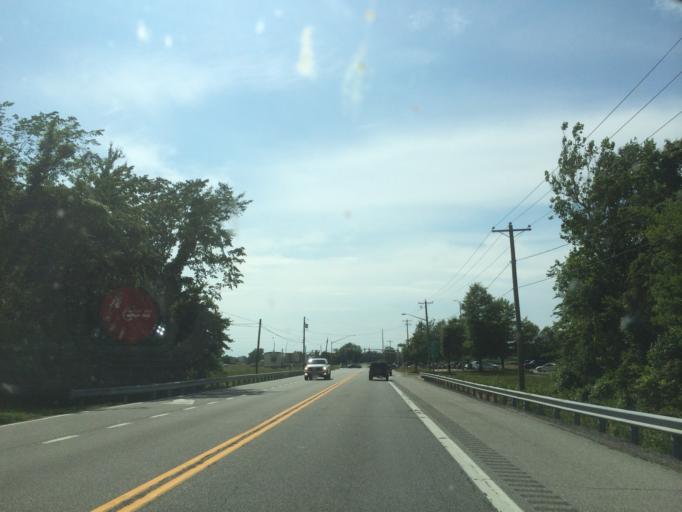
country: US
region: Maryland
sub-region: Queen Anne's County
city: Centreville
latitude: 38.9389
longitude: -76.0602
